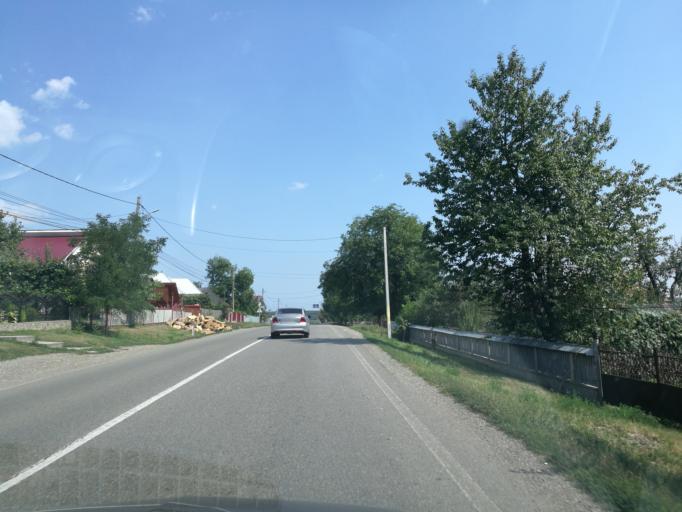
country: RO
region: Neamt
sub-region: Comuna Baltatesti
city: Valea Seaca
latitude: 47.1370
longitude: 26.3147
